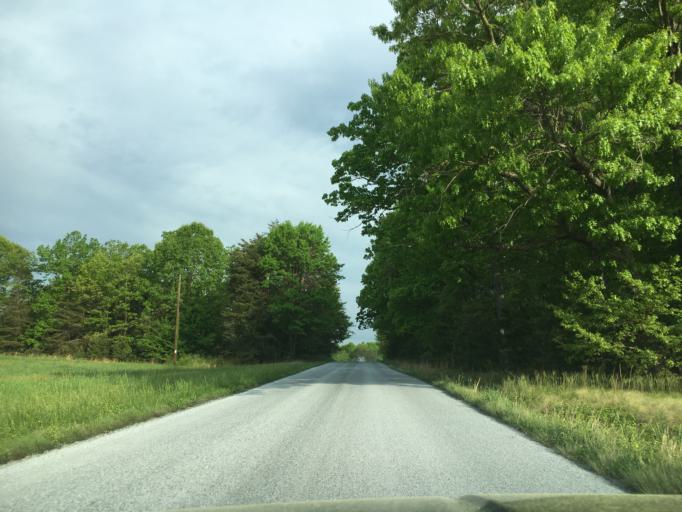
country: US
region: Virginia
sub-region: Campbell County
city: Brookneal
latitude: 36.9605
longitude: -78.9800
